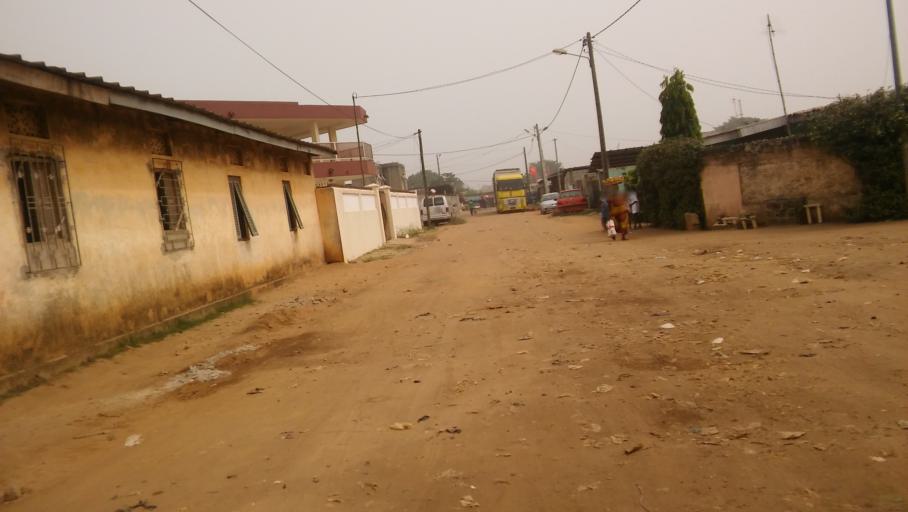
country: CI
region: Sud-Comoe
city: Grand-Bassam
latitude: 5.2133
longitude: -3.7336
